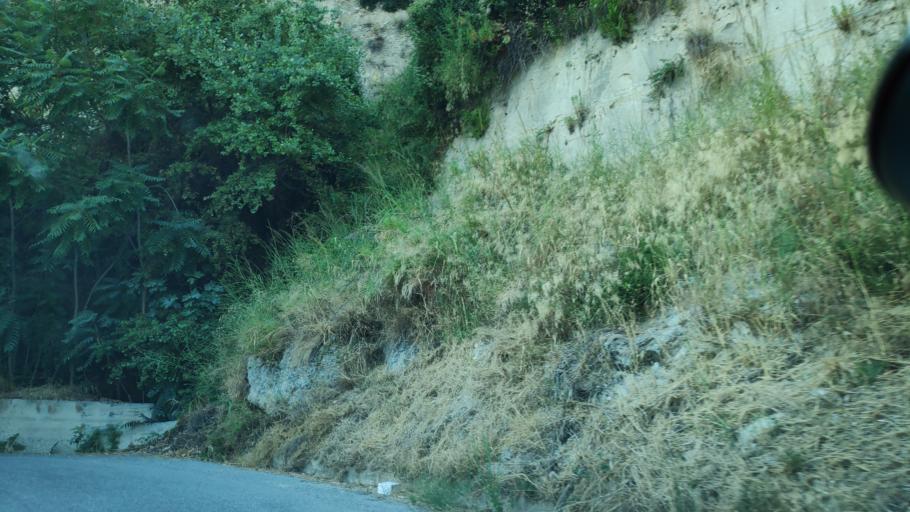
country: IT
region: Calabria
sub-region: Provincia di Catanzaro
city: Guardavalle
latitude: 38.5074
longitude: 16.5070
